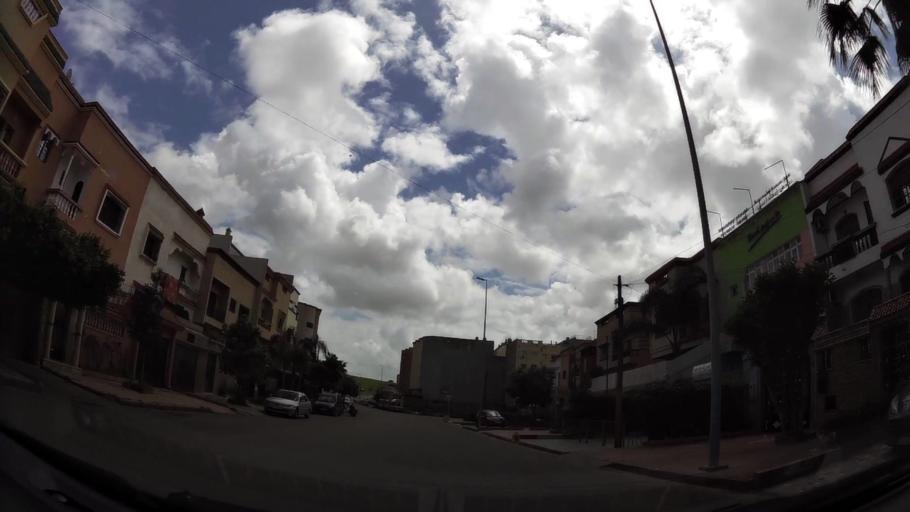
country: MA
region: Grand Casablanca
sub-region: Casablanca
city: Casablanca
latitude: 33.5304
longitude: -7.6024
